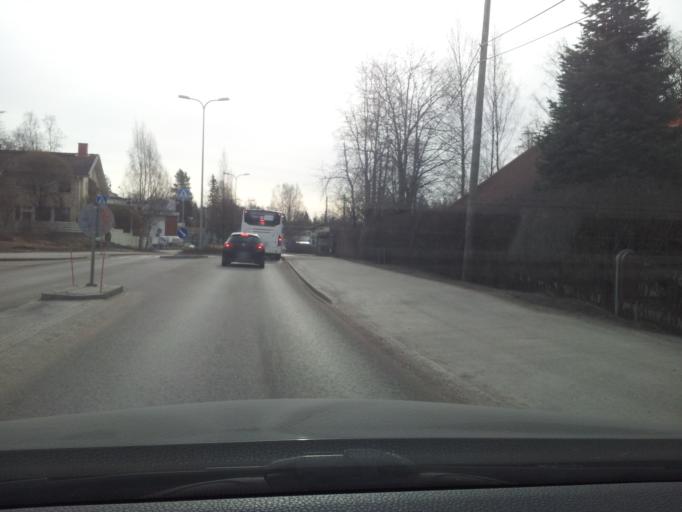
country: FI
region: Uusimaa
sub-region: Helsinki
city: Kilo
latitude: 60.1912
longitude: 24.7760
